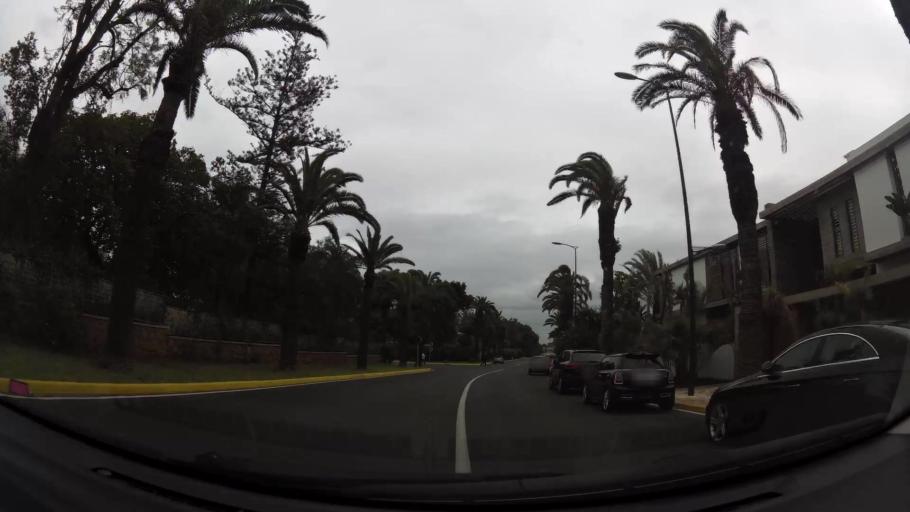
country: MA
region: Grand Casablanca
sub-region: Casablanca
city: Casablanca
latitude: 33.5844
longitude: -7.6611
